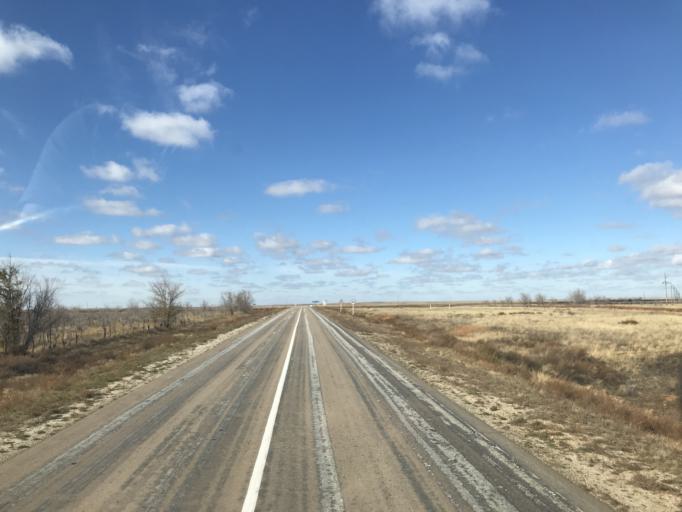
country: RU
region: Orenburg
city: Yasnyy
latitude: 50.4736
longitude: 60.1723
